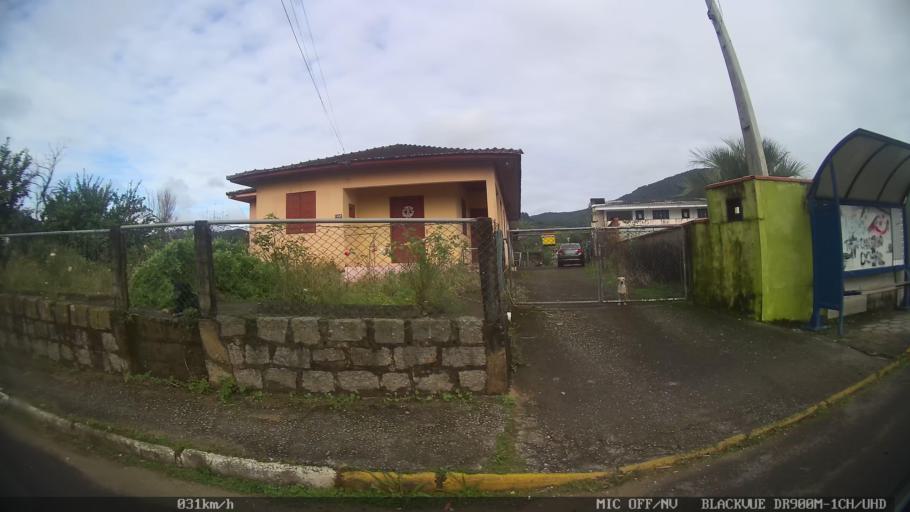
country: BR
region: Santa Catarina
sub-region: Biguacu
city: Biguacu
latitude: -27.5168
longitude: -48.6529
